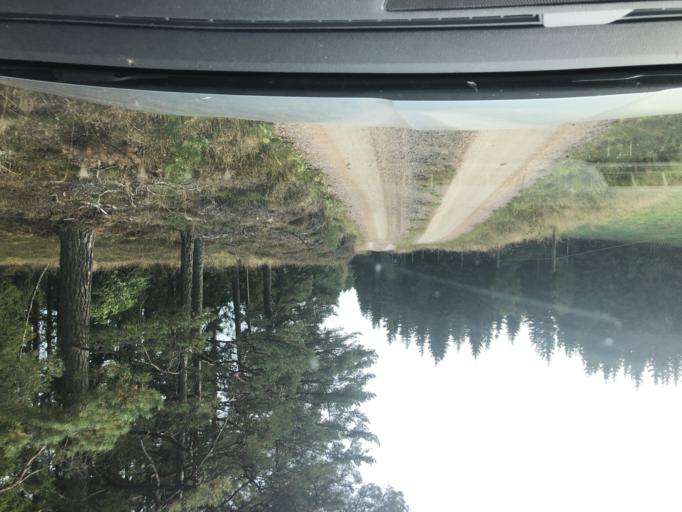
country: SE
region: Joenkoeping
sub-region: Vetlanda Kommun
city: Ekenassjon
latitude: 57.4990
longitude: 14.9019
